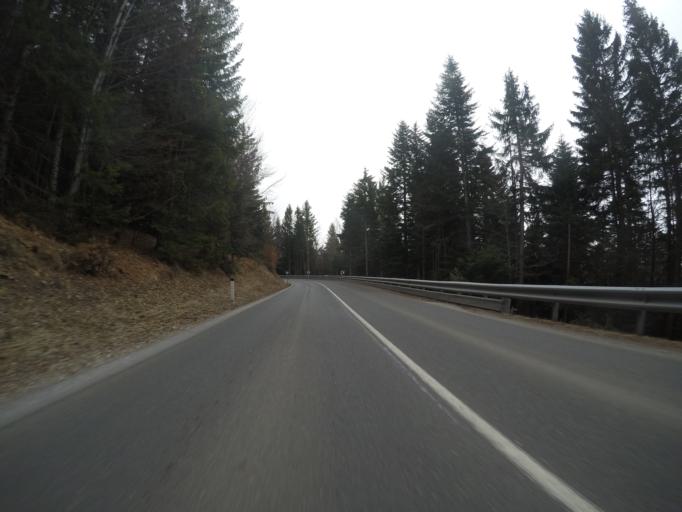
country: SI
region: Ruse
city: Ruse
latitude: 46.4934
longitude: 15.5198
